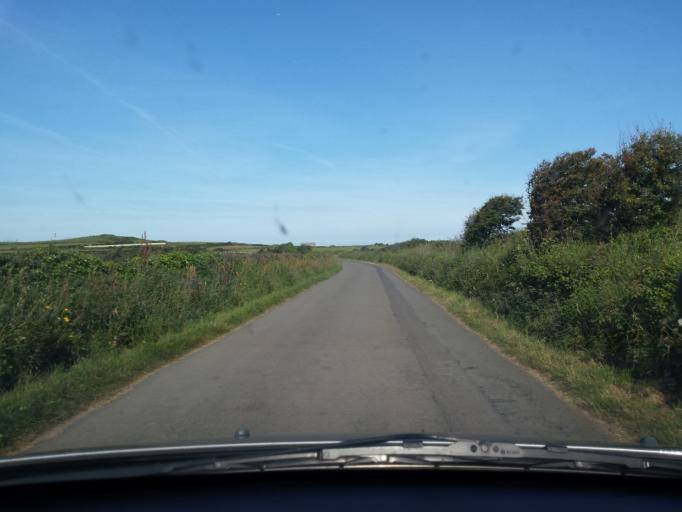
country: FR
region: Lower Normandy
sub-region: Departement de la Manche
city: Beaumont-Hague
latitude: 49.6759
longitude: -1.9298
